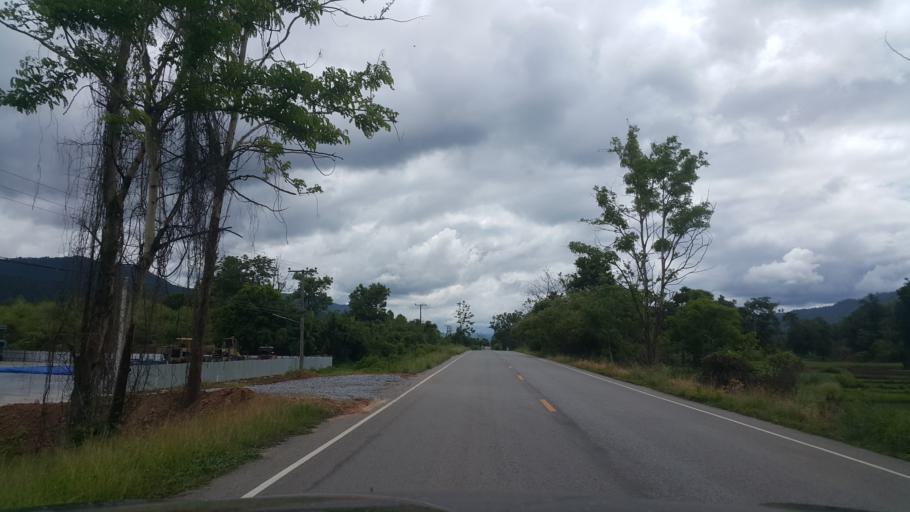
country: TH
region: Phitsanulok
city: Chat Trakan
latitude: 17.2927
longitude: 100.6491
